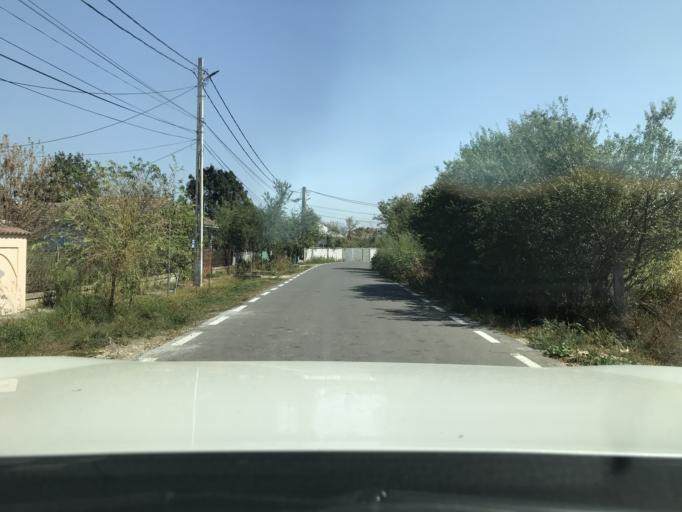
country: RO
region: Olt
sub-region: Comuna Falcoiu
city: Falcoiu
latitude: 44.2441
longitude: 24.3652
